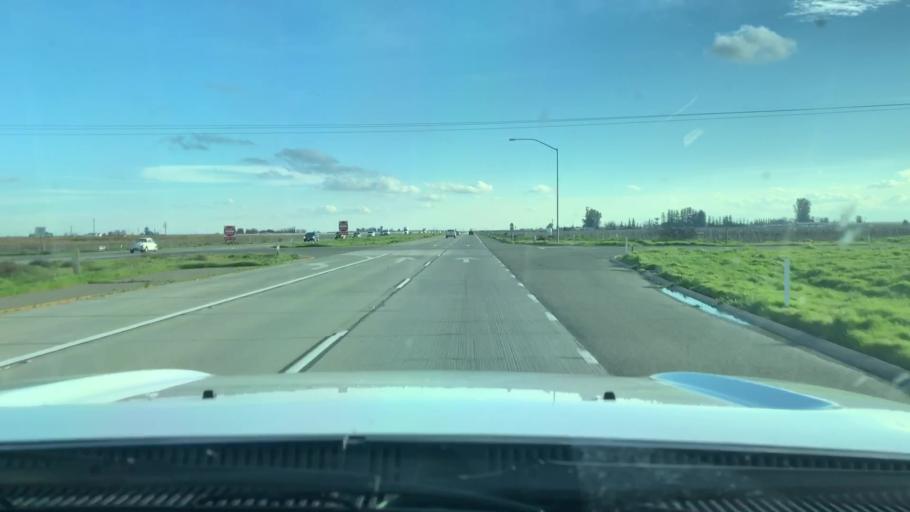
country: US
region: California
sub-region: Fresno County
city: Caruthers
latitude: 36.5623
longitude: -119.7863
